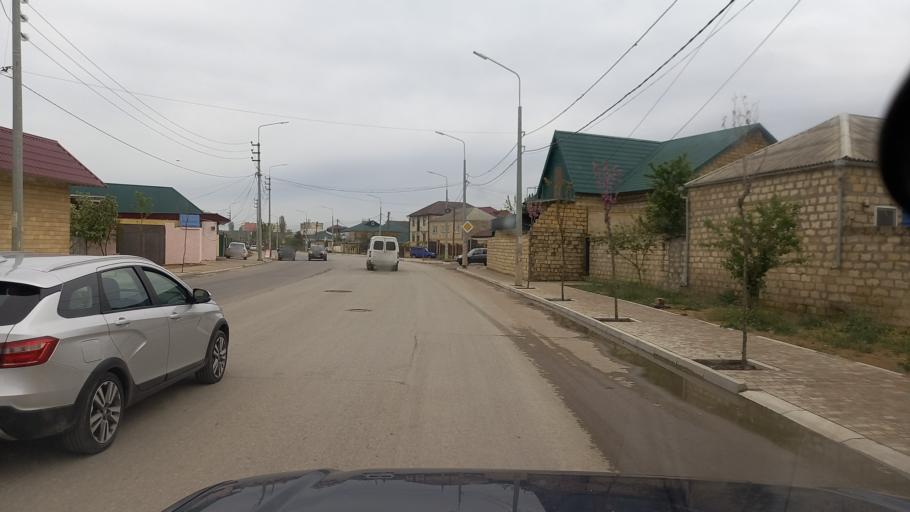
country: RU
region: Dagestan
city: Derbent
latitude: 42.0834
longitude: 48.2936
